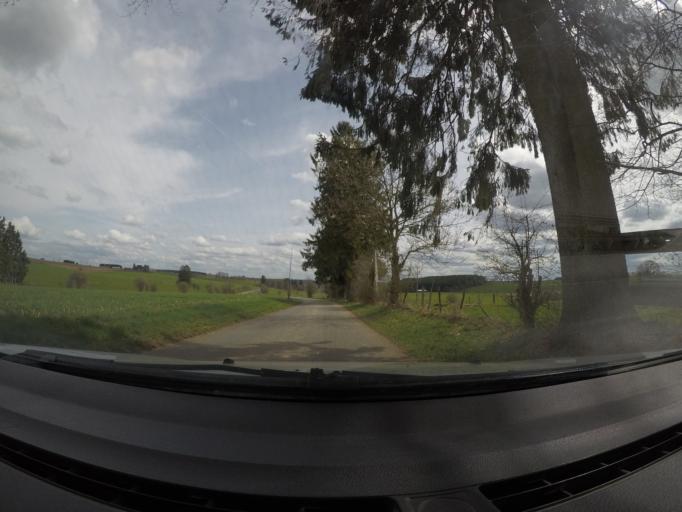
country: BE
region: Wallonia
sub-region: Province du Luxembourg
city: Neufchateau
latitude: 49.8243
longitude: 5.4594
